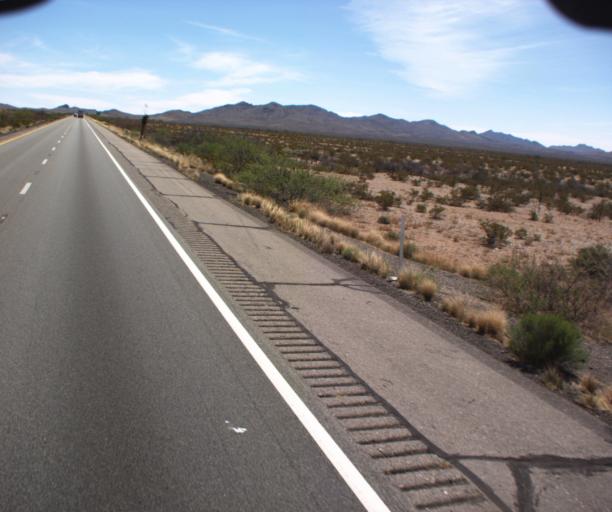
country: US
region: New Mexico
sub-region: Hidalgo County
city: Lordsburg
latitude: 32.2315
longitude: -109.0662
